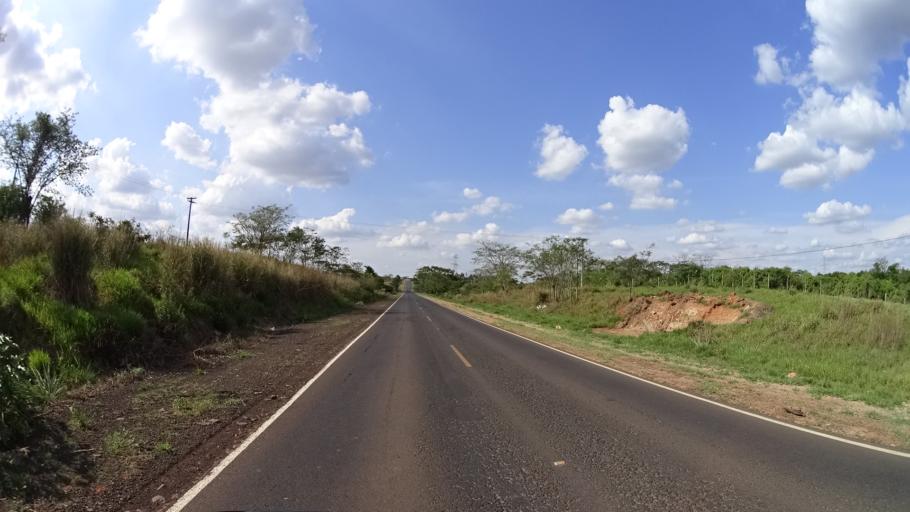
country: BR
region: Sao Paulo
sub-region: Urupes
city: Urupes
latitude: -21.0620
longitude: -49.2490
